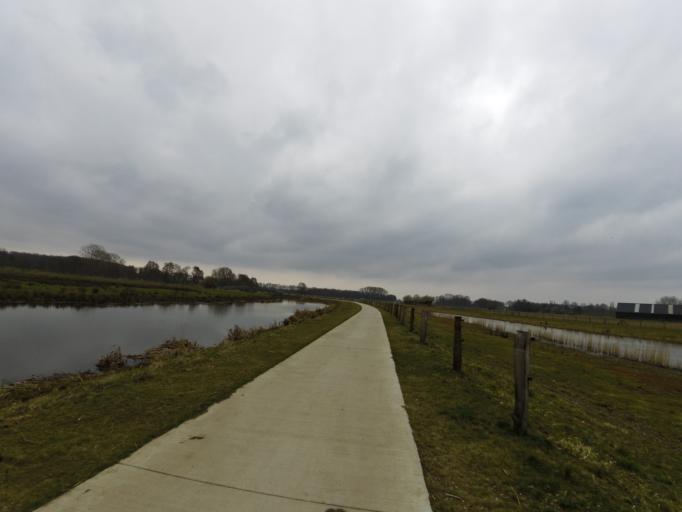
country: NL
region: Gelderland
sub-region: Oude IJsselstreek
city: Gendringen
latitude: 51.8758
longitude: 6.3889
